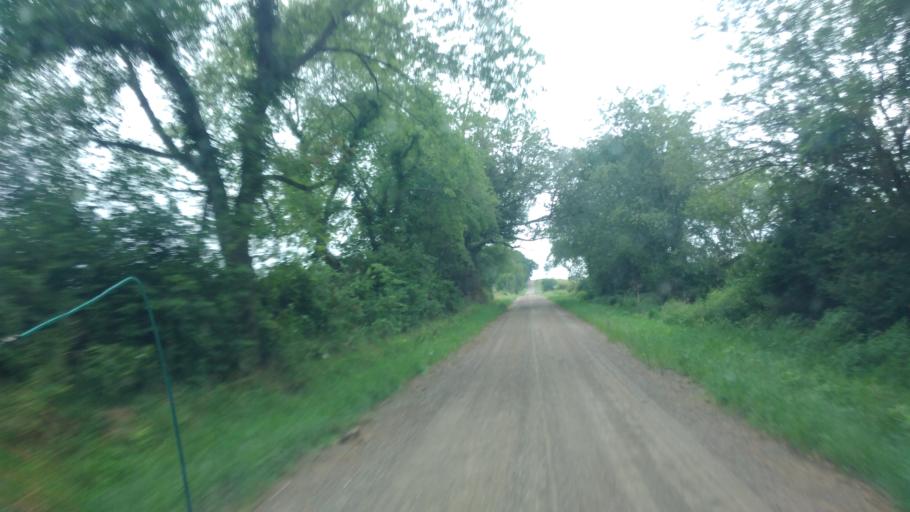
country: US
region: Ohio
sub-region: Knox County
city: Gambier
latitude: 40.2989
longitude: -82.3120
